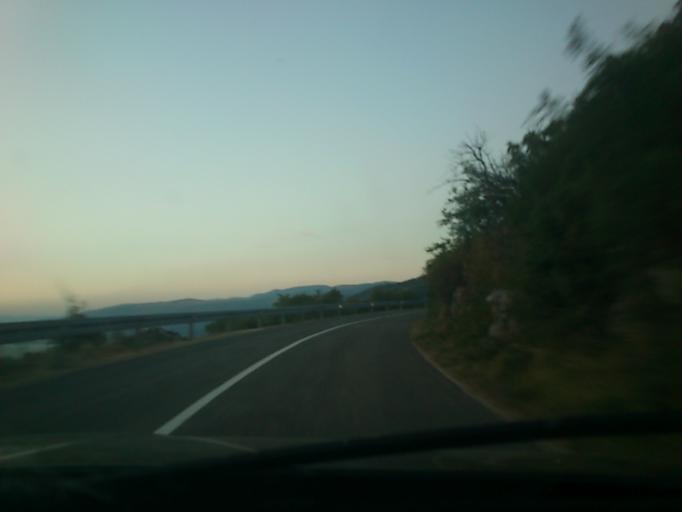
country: HR
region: Licko-Senjska
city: Senj
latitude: 44.9197
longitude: 14.9190
